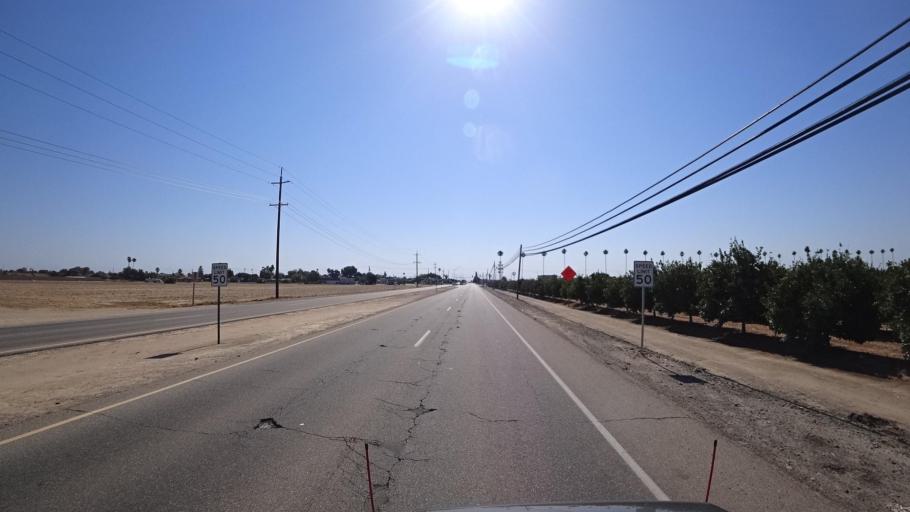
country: US
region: California
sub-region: Fresno County
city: Sunnyside
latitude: 36.7074
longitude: -119.7030
